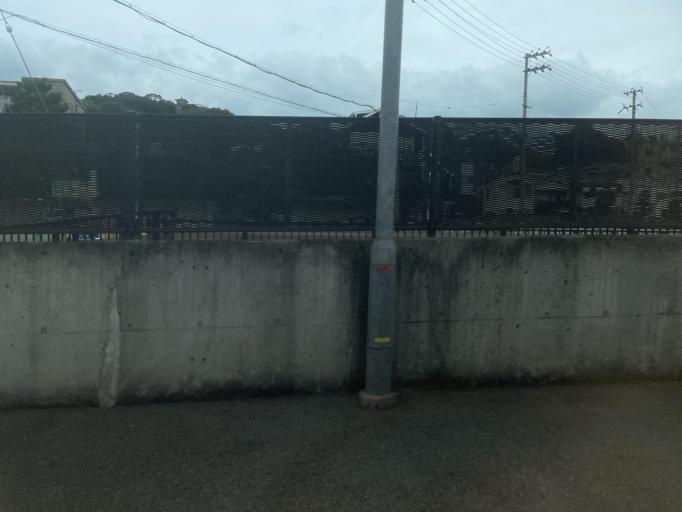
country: JP
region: Hyogo
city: Ashiya
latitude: 34.7245
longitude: 135.2515
